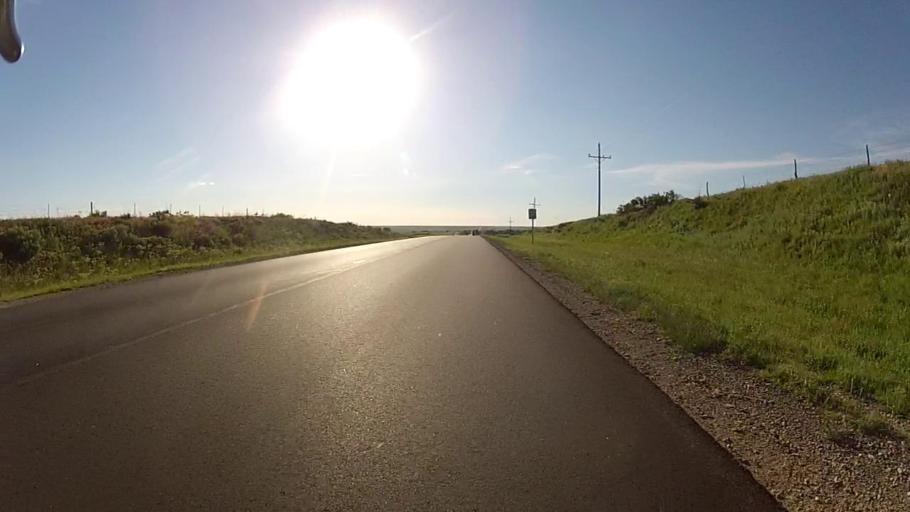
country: US
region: Kansas
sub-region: Comanche County
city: Coldwater
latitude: 37.2819
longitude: -99.0928
